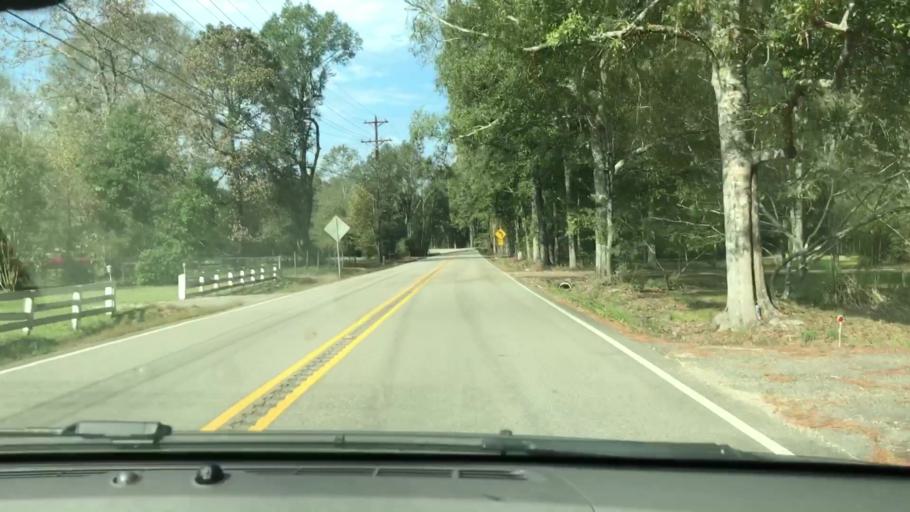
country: US
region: Louisiana
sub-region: Saint Tammany Parish
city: Abita Springs
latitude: 30.5334
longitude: -89.8833
